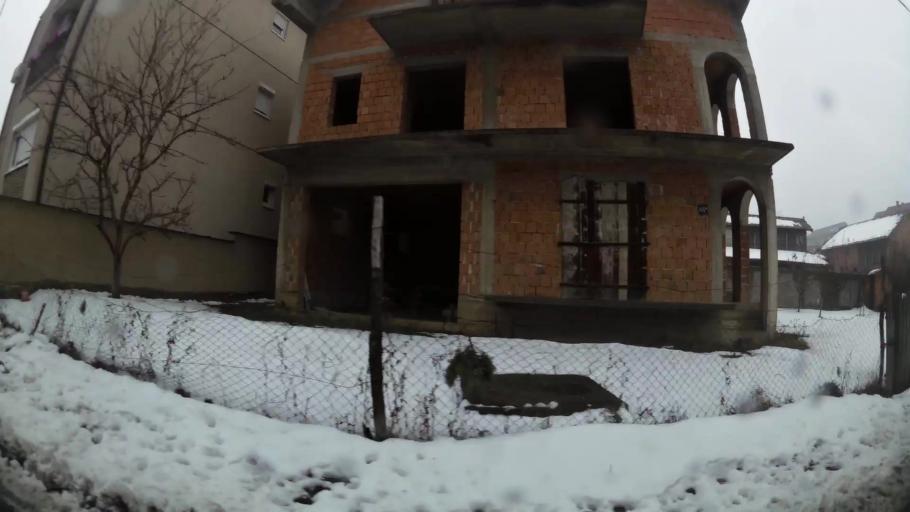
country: RS
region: Central Serbia
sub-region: Belgrade
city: Zvezdara
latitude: 44.7741
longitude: 20.5330
